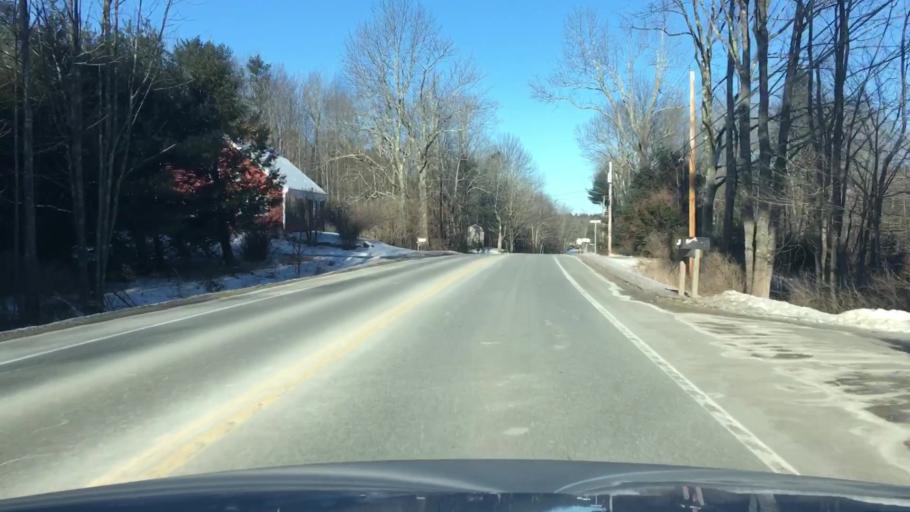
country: US
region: Maine
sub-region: Cumberland County
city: Freeport
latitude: 43.8789
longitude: -70.1095
